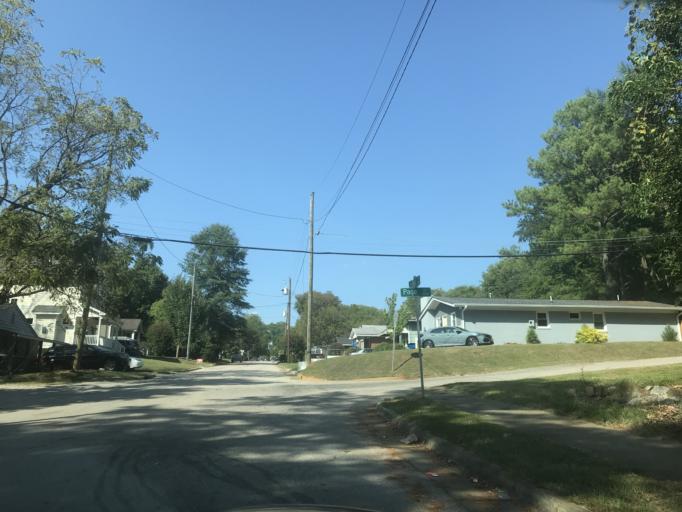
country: US
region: North Carolina
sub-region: Wake County
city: Raleigh
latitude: 35.7679
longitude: -78.6227
